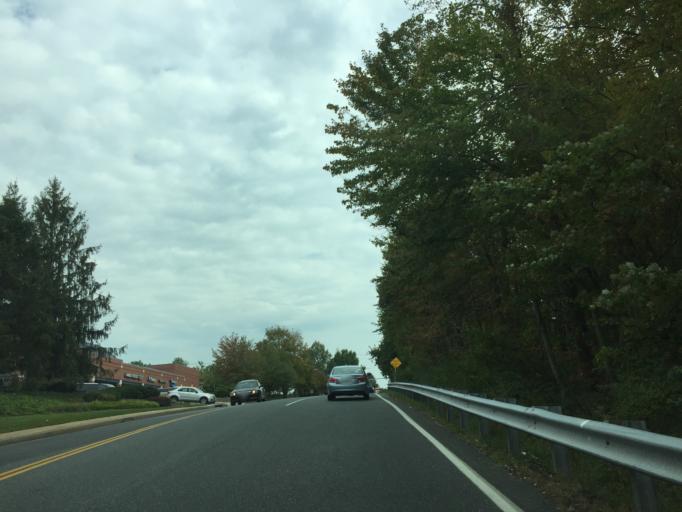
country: US
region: Maryland
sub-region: Harford County
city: Bel Air South
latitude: 39.4929
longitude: -76.3253
